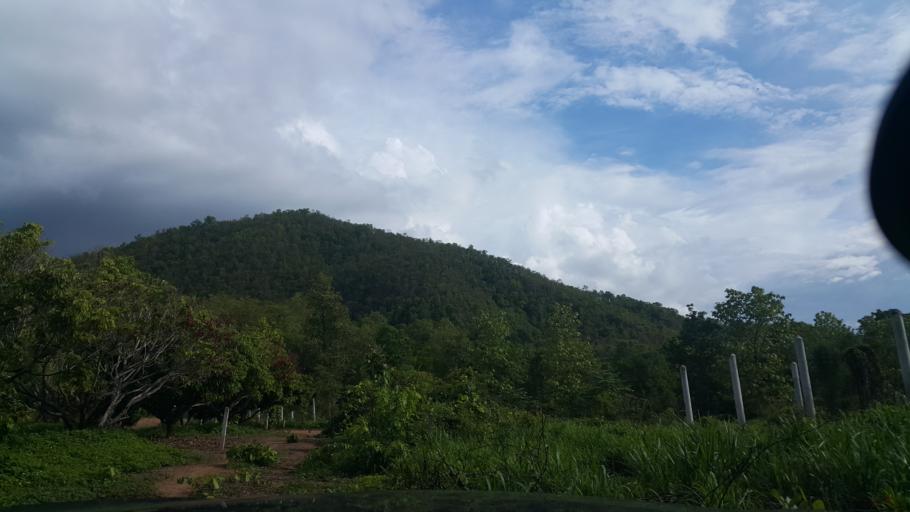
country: TH
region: Chiang Mai
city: Mae On
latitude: 18.7110
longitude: 99.2174
